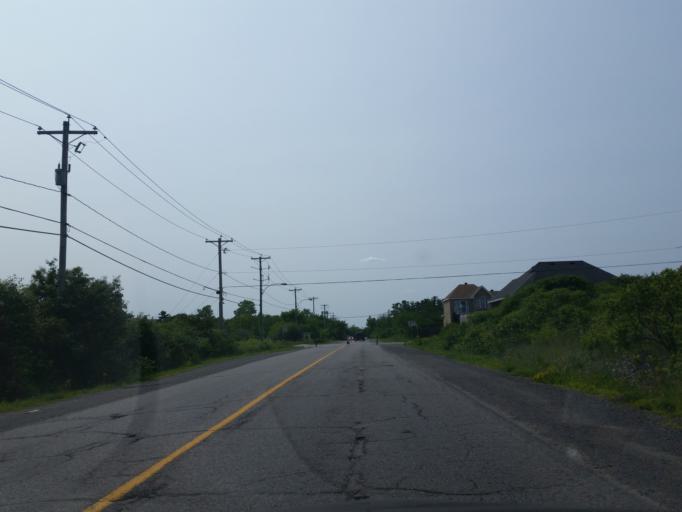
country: CA
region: Ontario
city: Bells Corners
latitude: 45.3860
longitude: -75.8289
